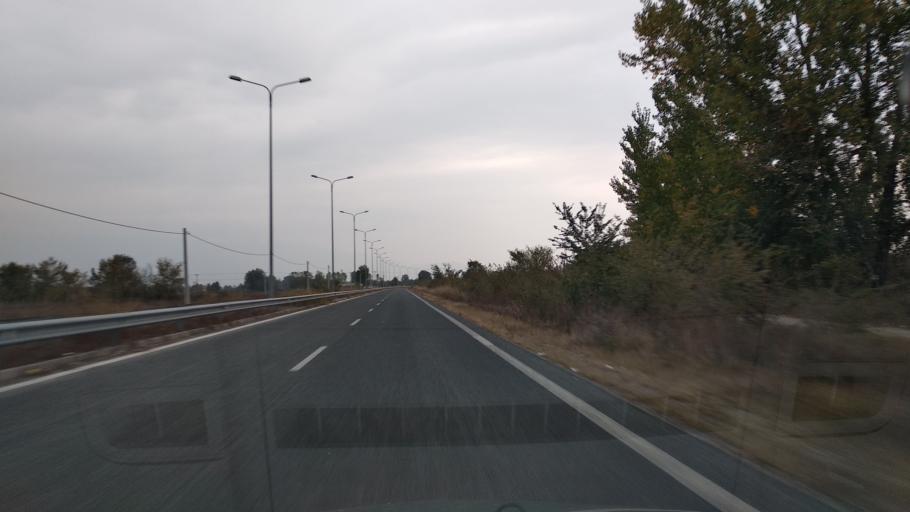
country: GR
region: Thessaly
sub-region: Trikala
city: Pyrgetos
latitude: 39.5338
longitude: 21.7400
